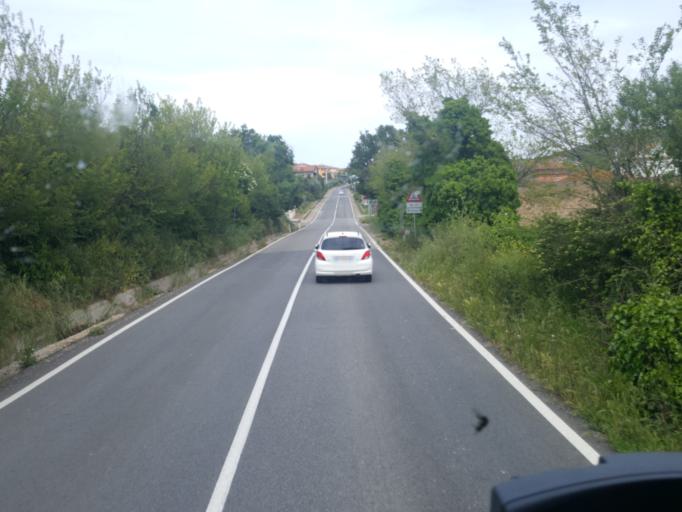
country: IT
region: Latium
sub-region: Provincia di Viterbo
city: Monte Romano
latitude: 42.2673
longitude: 11.8887
